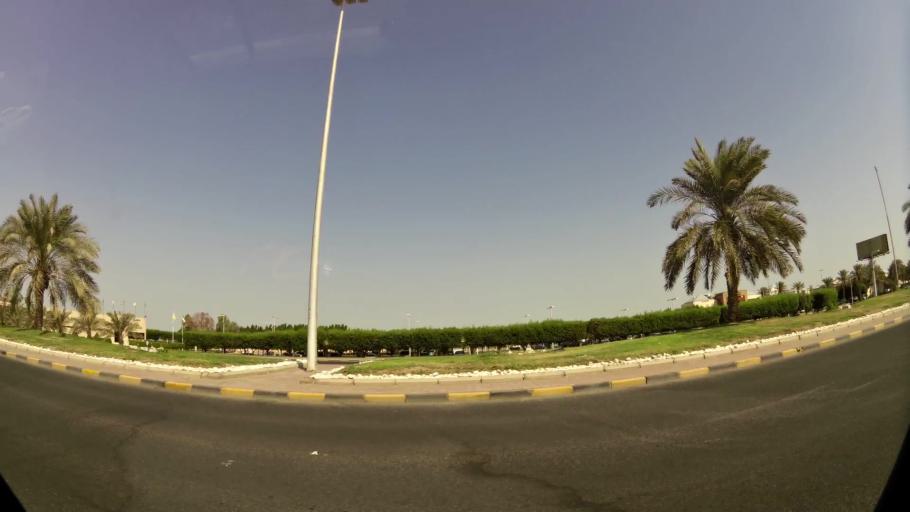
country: KW
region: Muhafazat Hawalli
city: Hawalli
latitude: 29.3436
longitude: 48.0452
